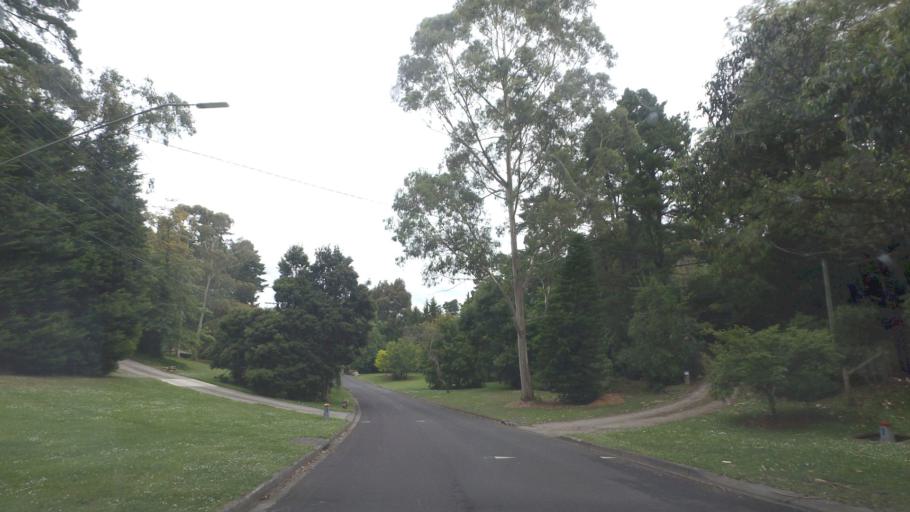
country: AU
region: Victoria
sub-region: Manningham
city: Park Orchards
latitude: -37.7832
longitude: 145.2136
